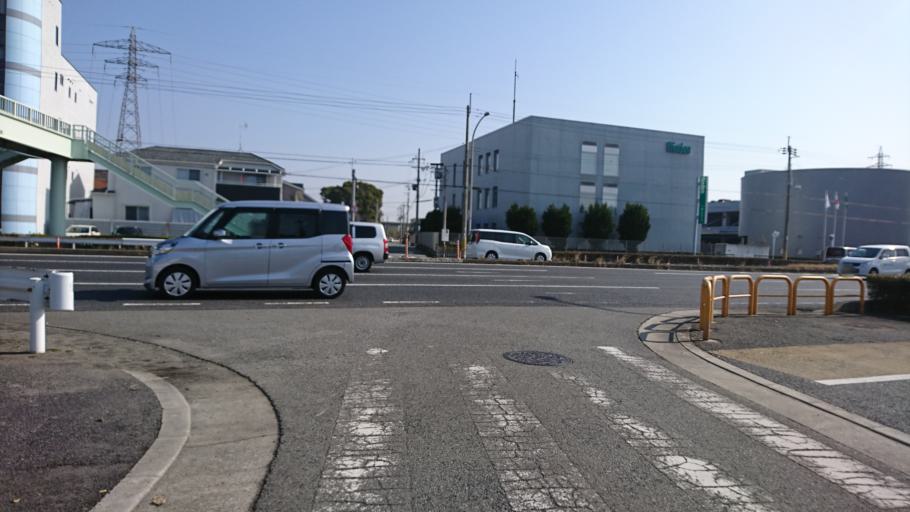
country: JP
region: Hyogo
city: Kakogawacho-honmachi
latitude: 34.7580
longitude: 134.8204
